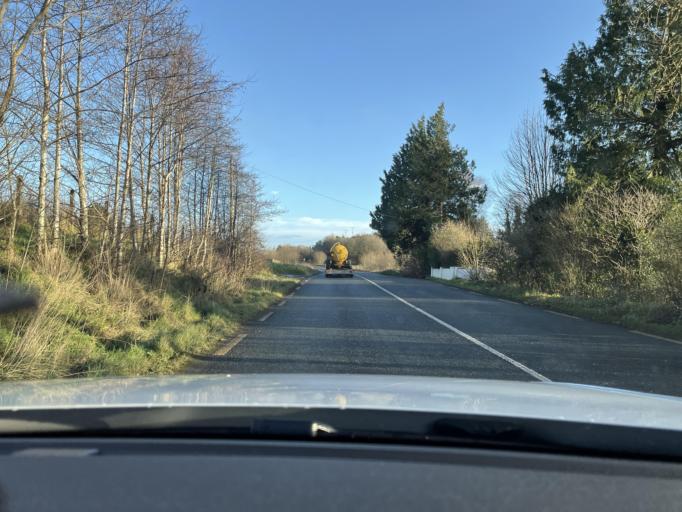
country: IE
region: Connaught
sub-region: County Leitrim
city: Manorhamilton
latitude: 54.1985
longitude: -8.1865
